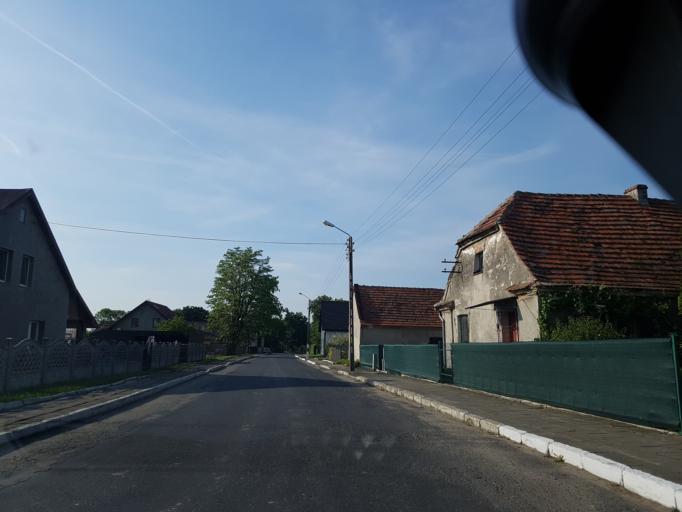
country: PL
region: Lower Silesian Voivodeship
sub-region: Powiat strzelinski
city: Wiazow
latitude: 50.8516
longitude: 17.1861
